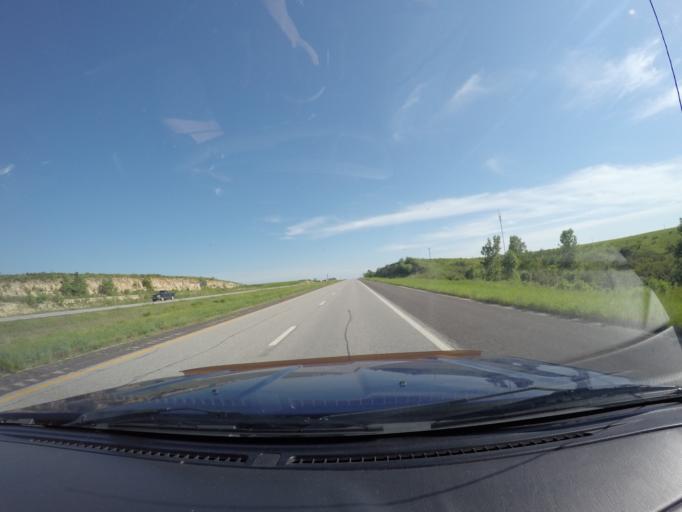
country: US
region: Kansas
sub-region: Riley County
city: Manhattan
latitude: 39.0706
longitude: -96.5385
